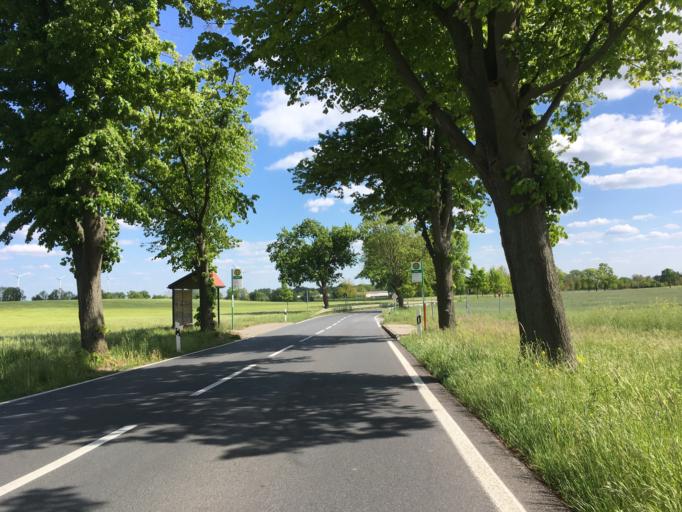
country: DE
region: Brandenburg
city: Ahrensfelde
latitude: 52.6140
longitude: 13.6172
